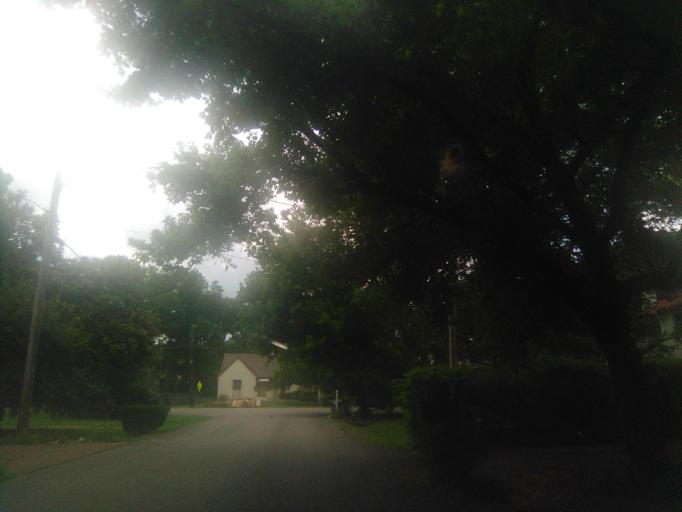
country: US
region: Tennessee
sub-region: Davidson County
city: Belle Meade
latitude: 36.1156
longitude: -86.8392
